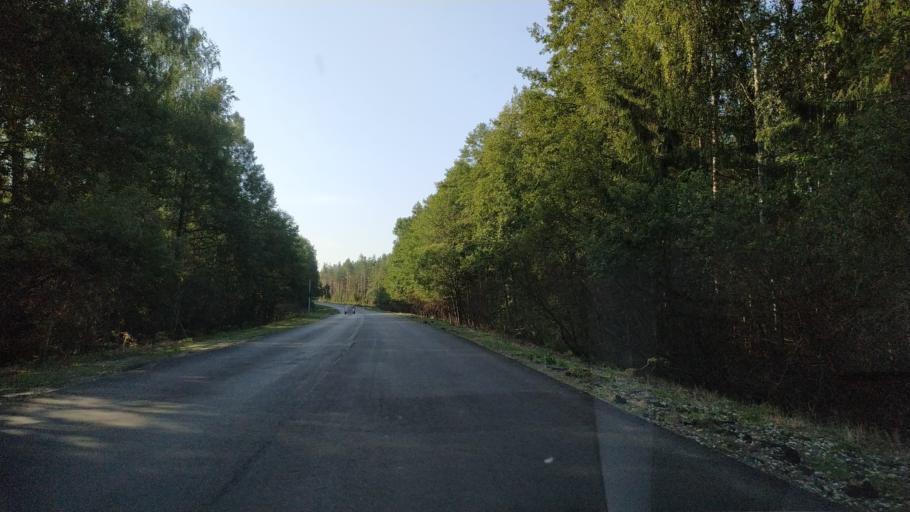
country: RU
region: Moskovskaya
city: Dmitrovskiy Pogost
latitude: 55.4152
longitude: 39.7486
